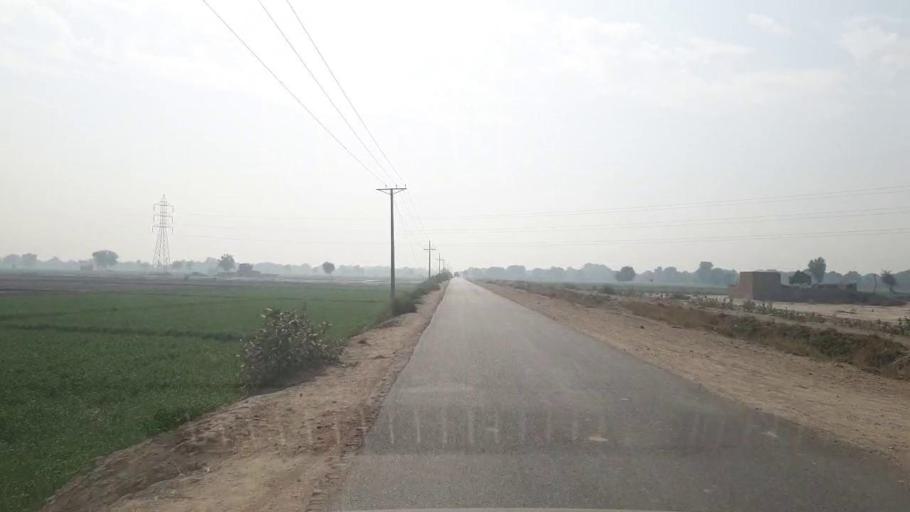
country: PK
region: Sindh
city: Hala
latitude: 25.8013
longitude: 68.4373
